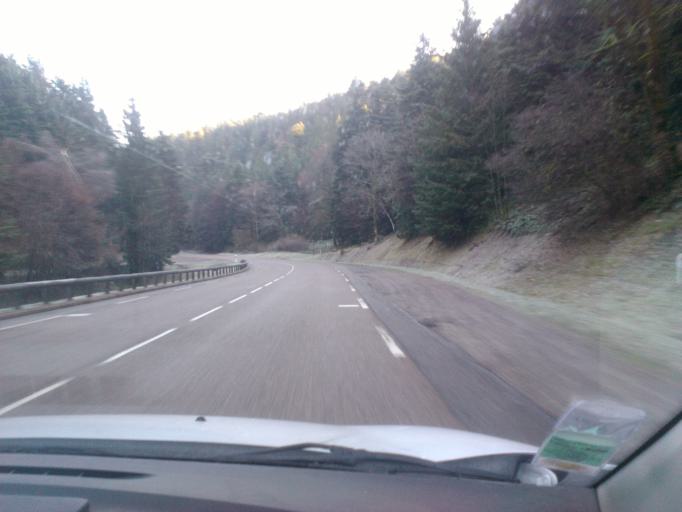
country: FR
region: Lorraine
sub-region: Departement des Vosges
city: Remiremont
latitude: 47.9891
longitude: 6.5664
